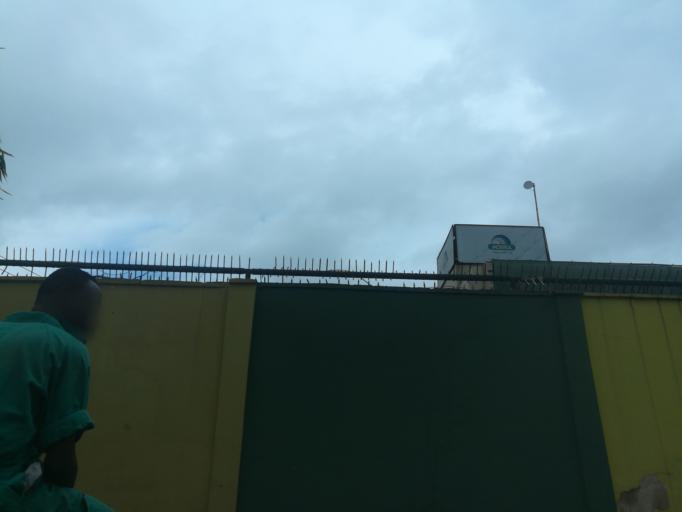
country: NG
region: Lagos
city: Agege
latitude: 6.6134
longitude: 3.3416
